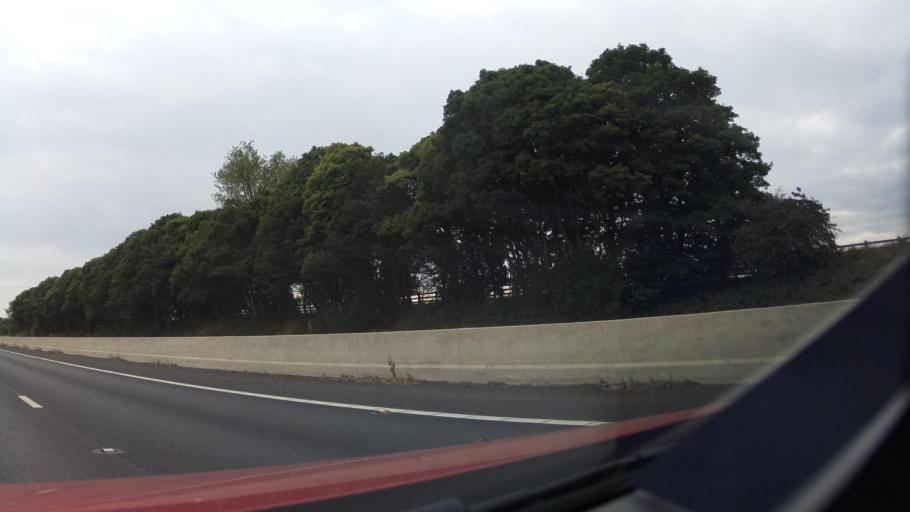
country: GB
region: England
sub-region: Darlington
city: Coatham Mundeville
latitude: 54.6041
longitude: -1.5372
